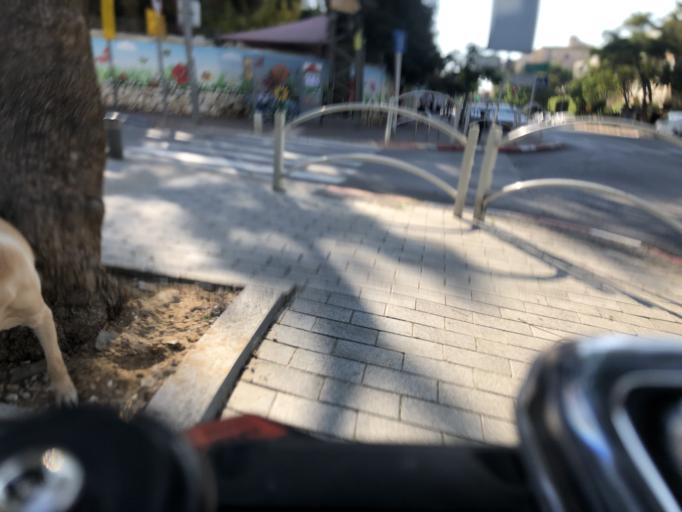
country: IL
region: Tel Aviv
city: Giv`atayim
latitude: 32.0687
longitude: 34.8086
